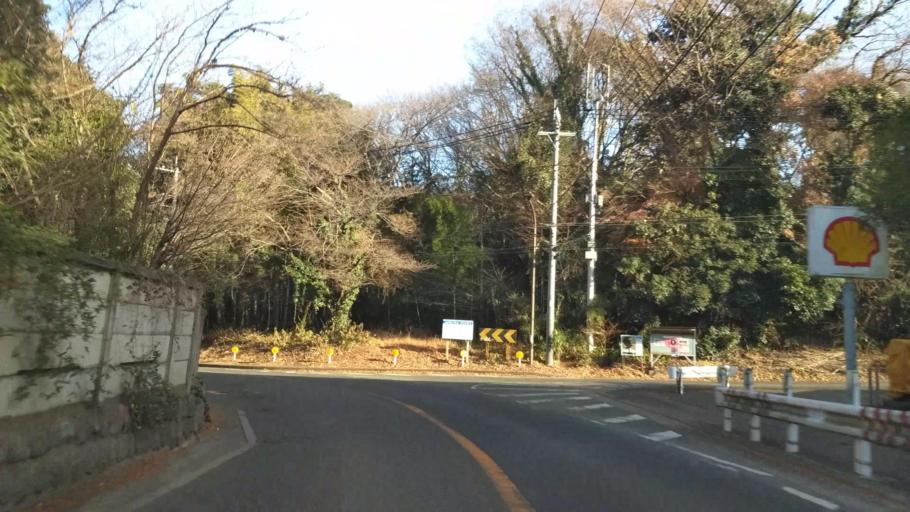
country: JP
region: Kanagawa
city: Ninomiya
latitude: 35.3456
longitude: 139.2715
